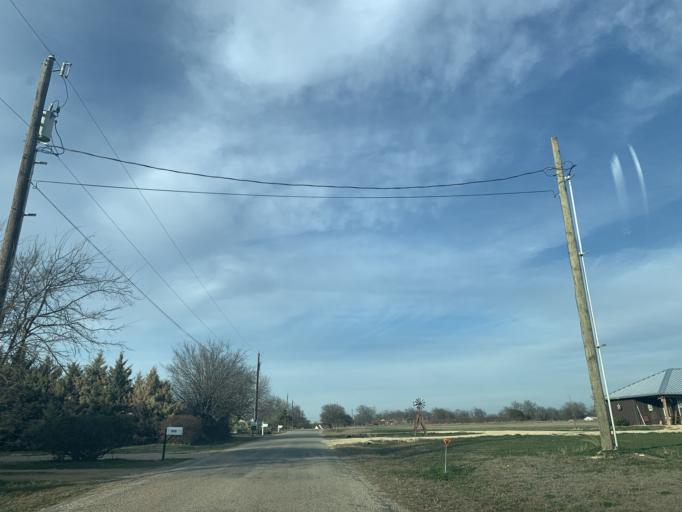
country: US
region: Texas
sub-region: Bell County
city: Salado
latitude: 30.8798
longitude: -97.5812
